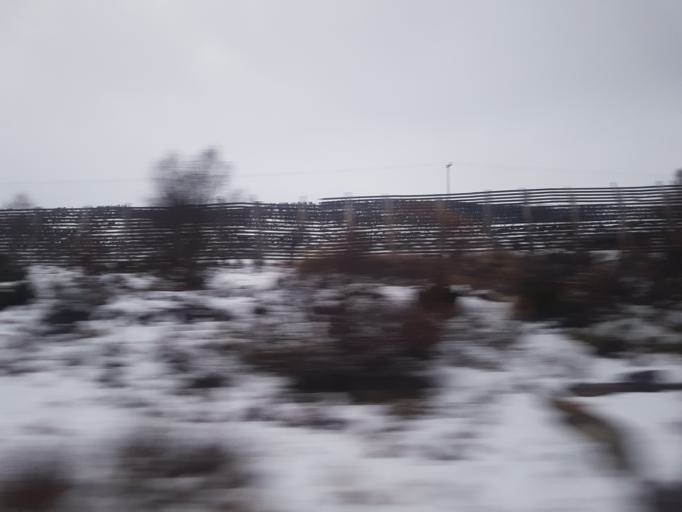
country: NO
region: Sor-Trondelag
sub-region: Oppdal
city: Oppdal
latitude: 62.2837
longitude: 9.5949
